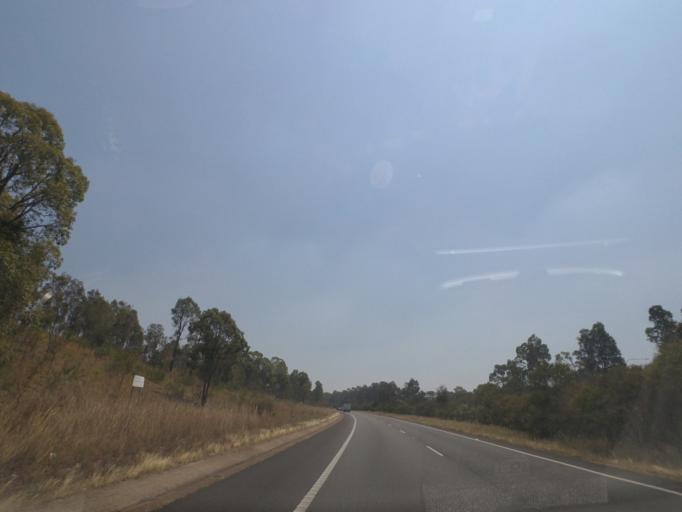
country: AU
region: New South Wales
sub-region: Newcastle
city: Beresfield
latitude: -32.8378
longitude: 151.6348
